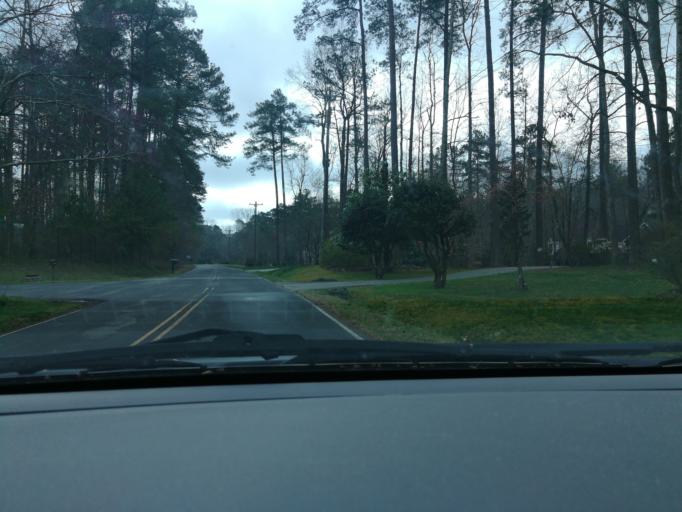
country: US
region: North Carolina
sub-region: Durham County
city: Durham
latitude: 36.0695
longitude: -78.9739
